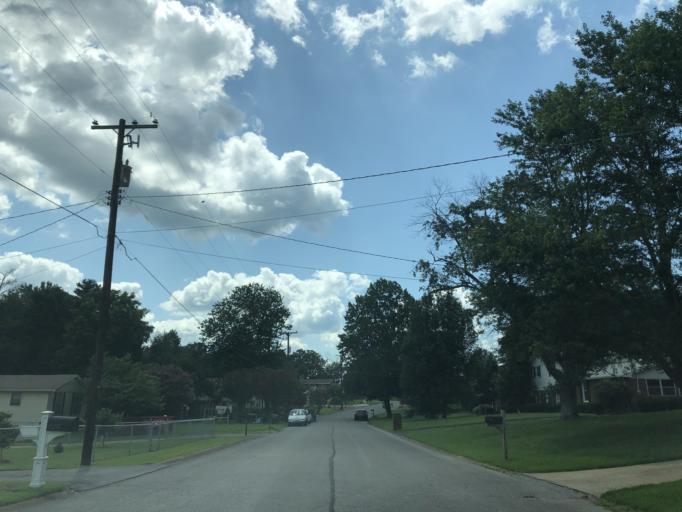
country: US
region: Tennessee
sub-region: Davidson County
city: Lakewood
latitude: 36.2101
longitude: -86.6037
